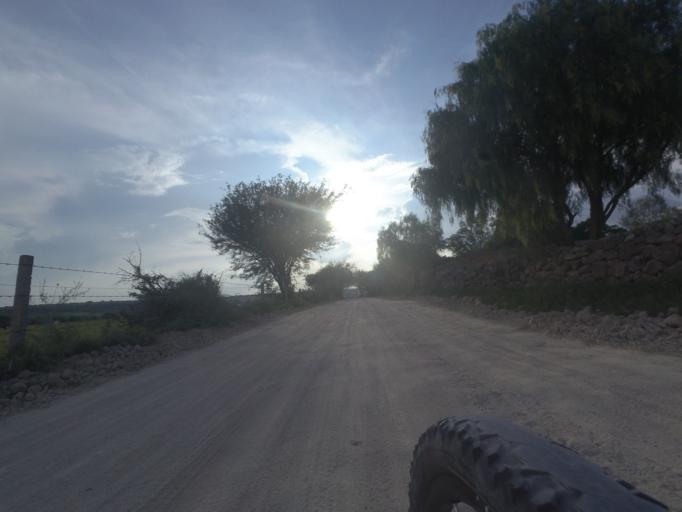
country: MX
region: Aguascalientes
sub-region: Aguascalientes
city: La Loma de los Negritos
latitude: 21.7755
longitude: -102.3696
